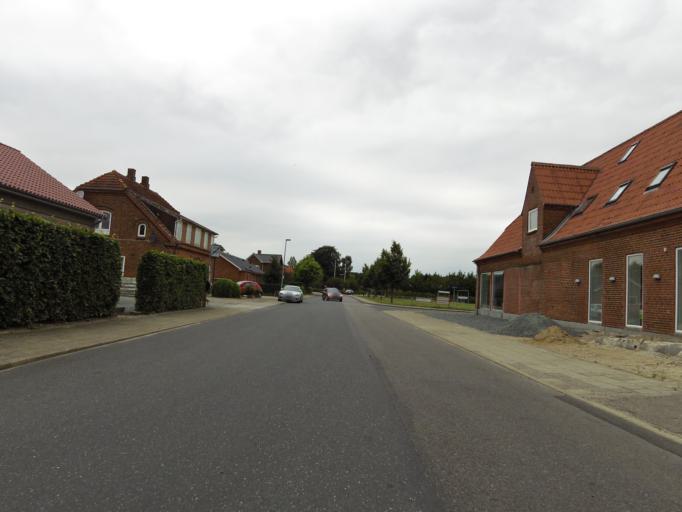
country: DK
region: South Denmark
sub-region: Tonder Kommune
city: Logumkloster
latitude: 55.0746
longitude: 8.9309
